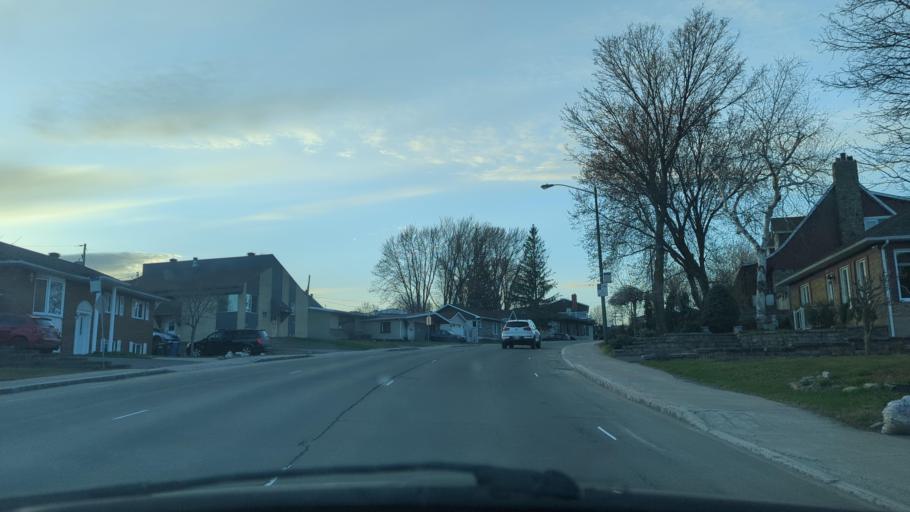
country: CA
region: Quebec
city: Quebec
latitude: 46.8504
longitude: -71.2621
